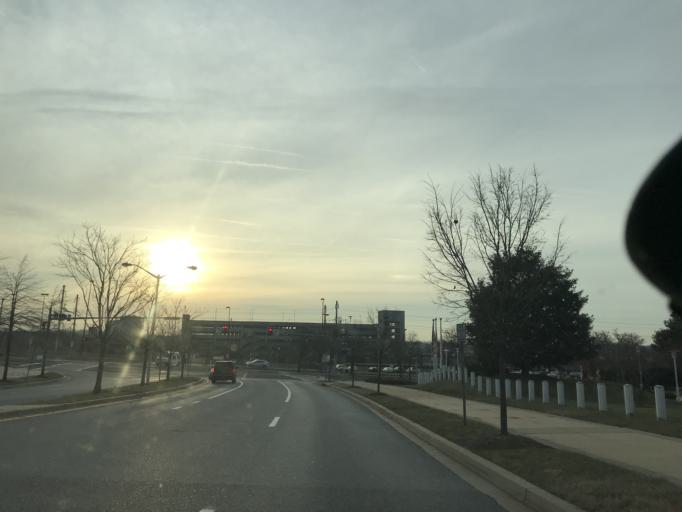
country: US
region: Maryland
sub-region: Prince George's County
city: Woodlawn
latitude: 38.9504
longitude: -76.8727
